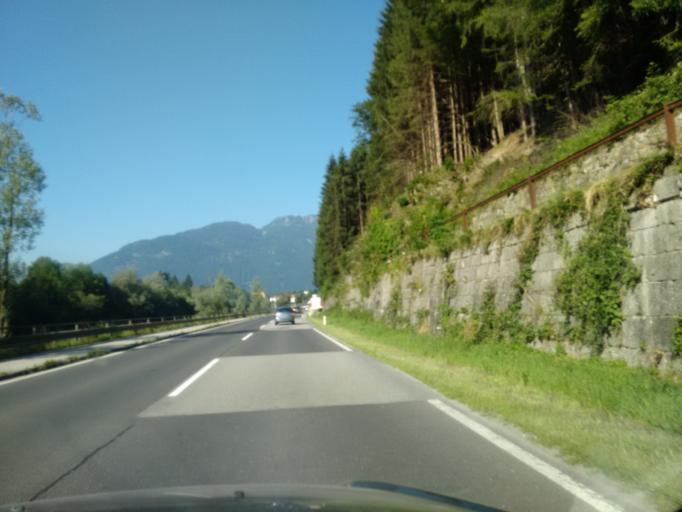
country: AT
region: Upper Austria
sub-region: Politischer Bezirk Gmunden
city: Bad Ischl
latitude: 47.7224
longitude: 13.6430
